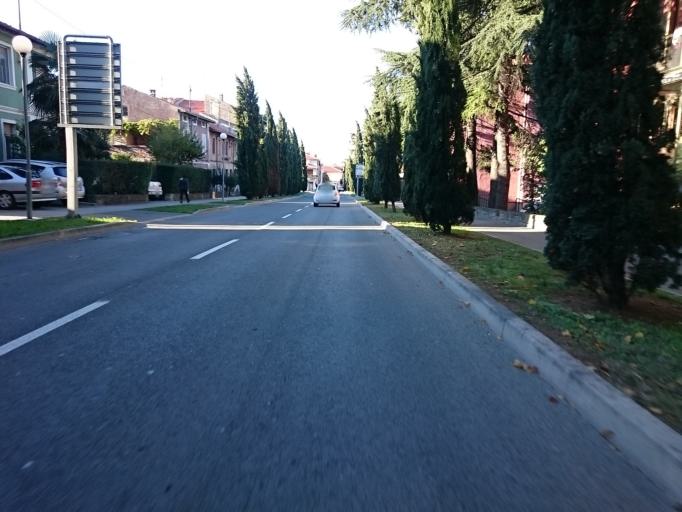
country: SI
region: Izola-Isola
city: Izola
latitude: 45.5350
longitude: 13.6628
